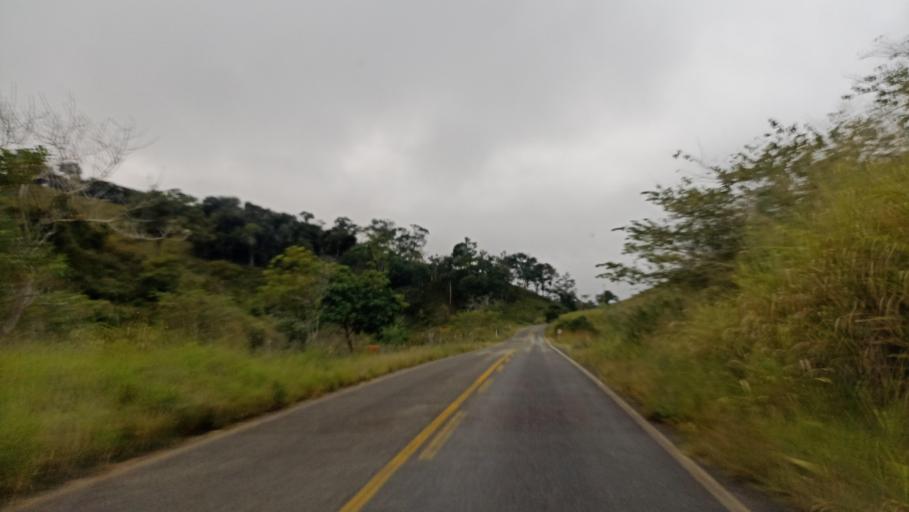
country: BR
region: Bahia
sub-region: Itanhem
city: Itanhem
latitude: -16.6920
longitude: -40.5158
